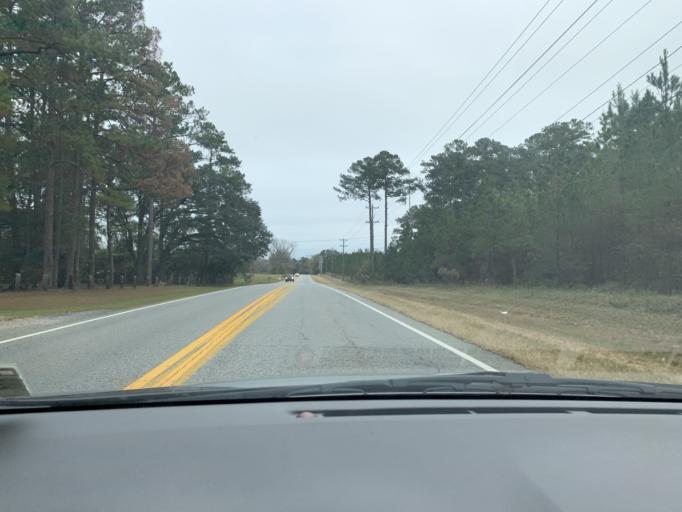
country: US
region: Georgia
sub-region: Thomas County
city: Thomasville
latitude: 30.8579
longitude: -83.9187
